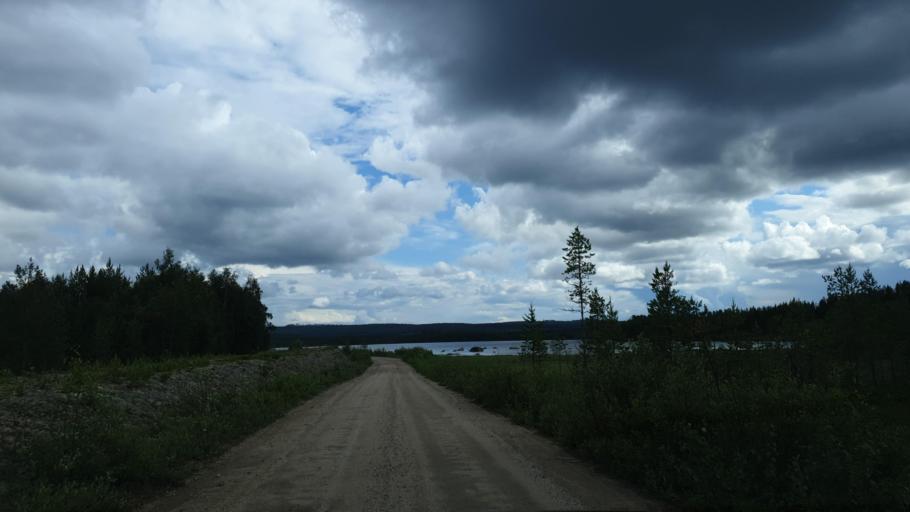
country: SE
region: Jaemtland
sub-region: Harjedalens Kommun
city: Sveg
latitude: 62.0435
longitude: 14.4821
